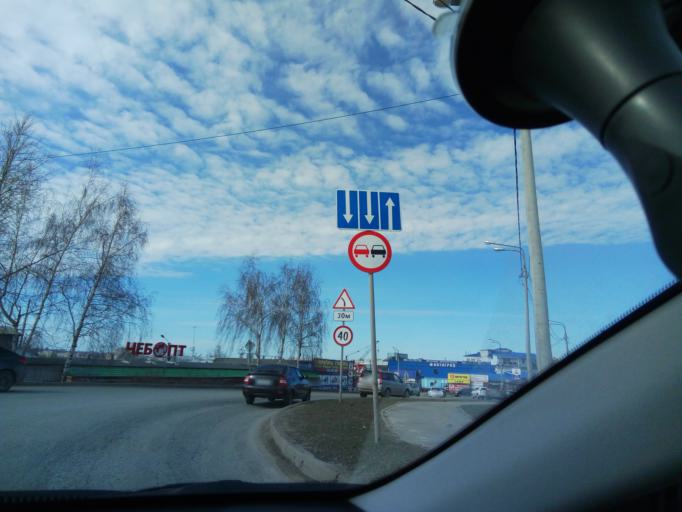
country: RU
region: Chuvashia
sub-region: Cheboksarskiy Rayon
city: Cheboksary
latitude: 56.1016
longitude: 47.2529
